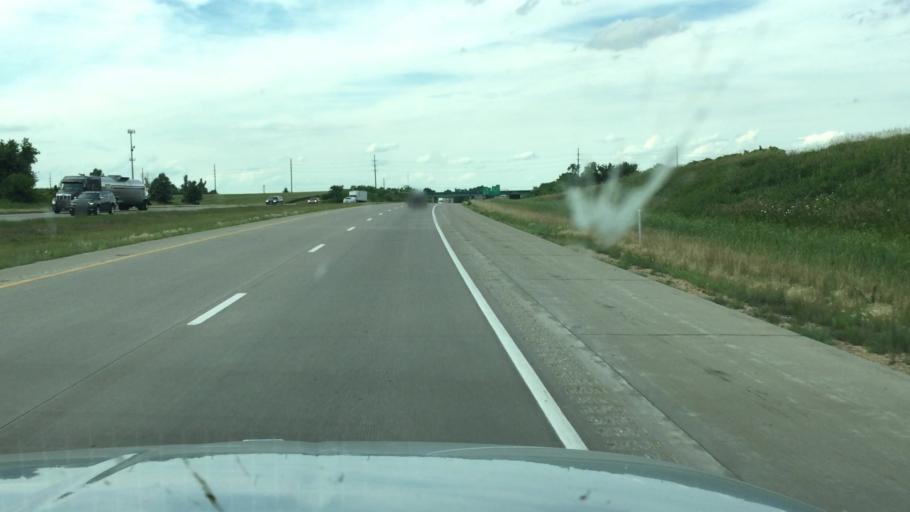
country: US
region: Iowa
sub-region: Scott County
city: Walcott
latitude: 41.5659
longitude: -90.6788
